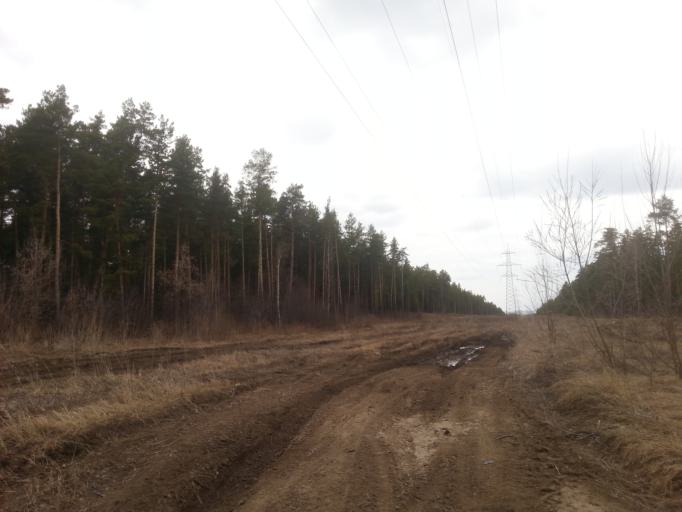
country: RU
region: Altai Krai
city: Yuzhnyy
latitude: 53.2893
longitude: 83.7277
